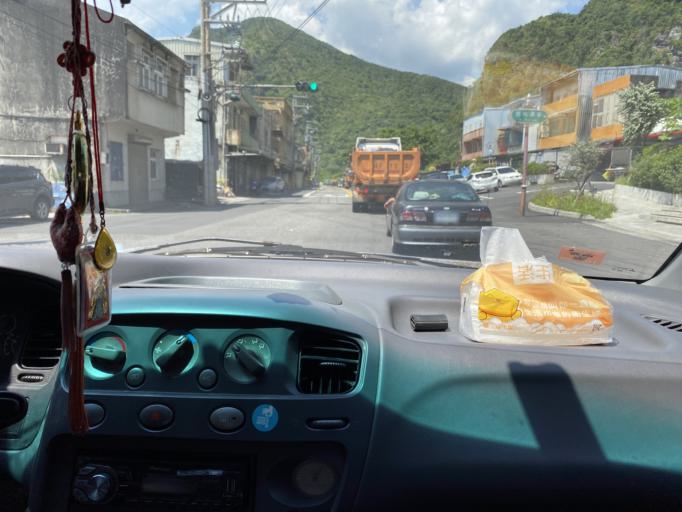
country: TW
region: Taiwan
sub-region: Yilan
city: Yilan
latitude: 24.9419
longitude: 121.8986
